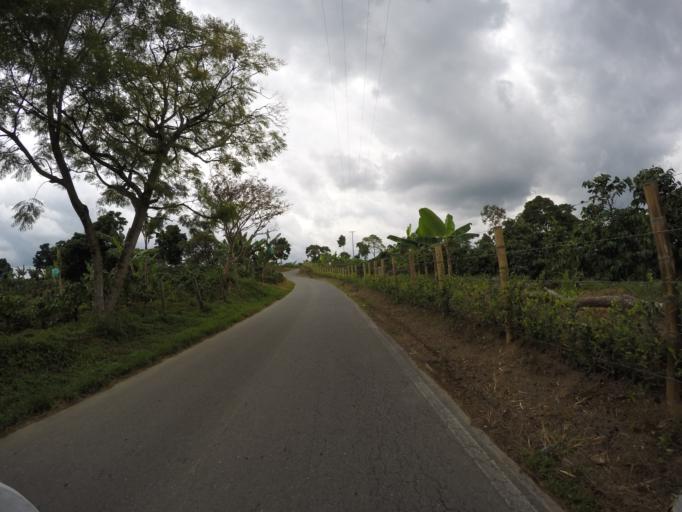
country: CO
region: Quindio
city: Quimbaya
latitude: 4.6097
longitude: -75.7170
